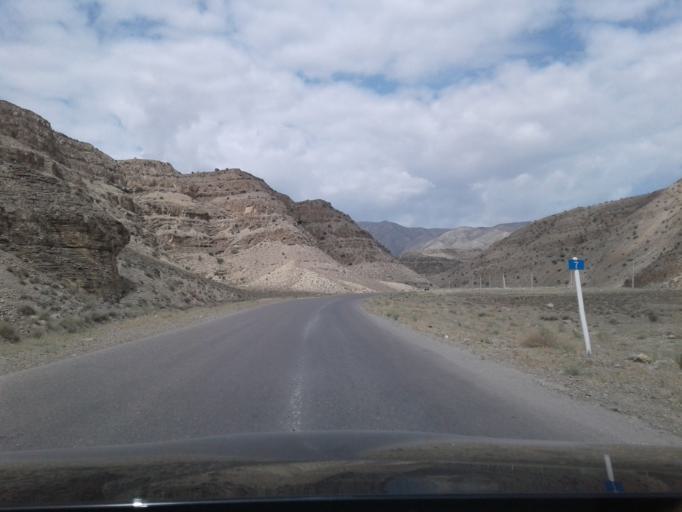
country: TM
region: Ahal
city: Baharly
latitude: 38.5012
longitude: 57.1005
